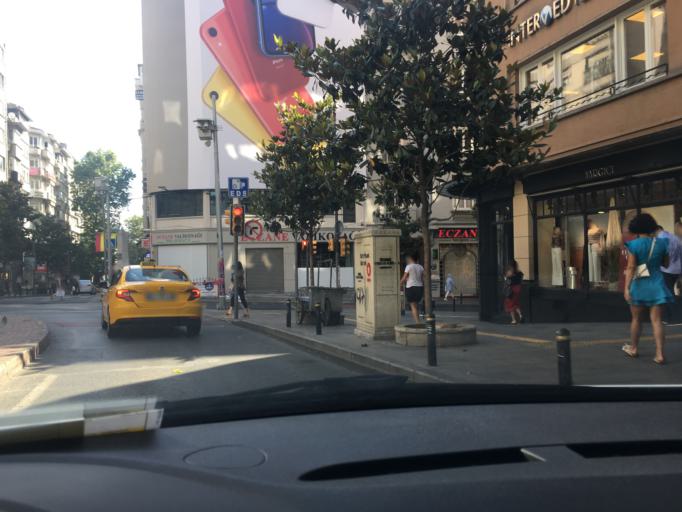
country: TR
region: Istanbul
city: Sisli
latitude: 41.0515
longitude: 28.9913
